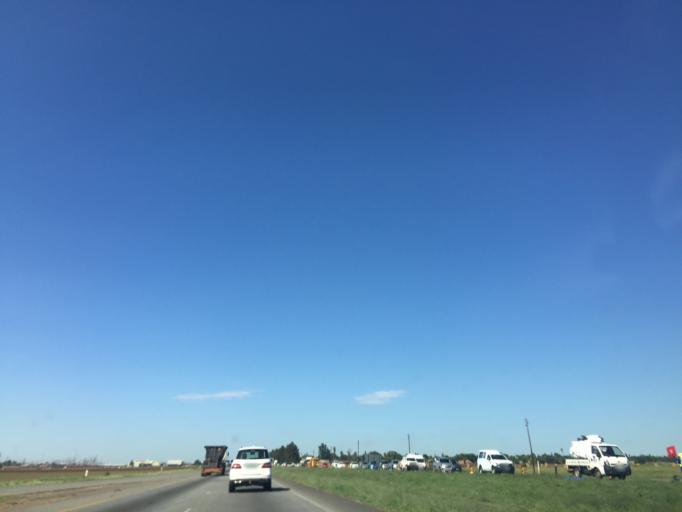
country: ZA
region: Gauteng
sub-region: Sedibeng District Municipality
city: Vereeniging
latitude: -26.6284
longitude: 27.9620
